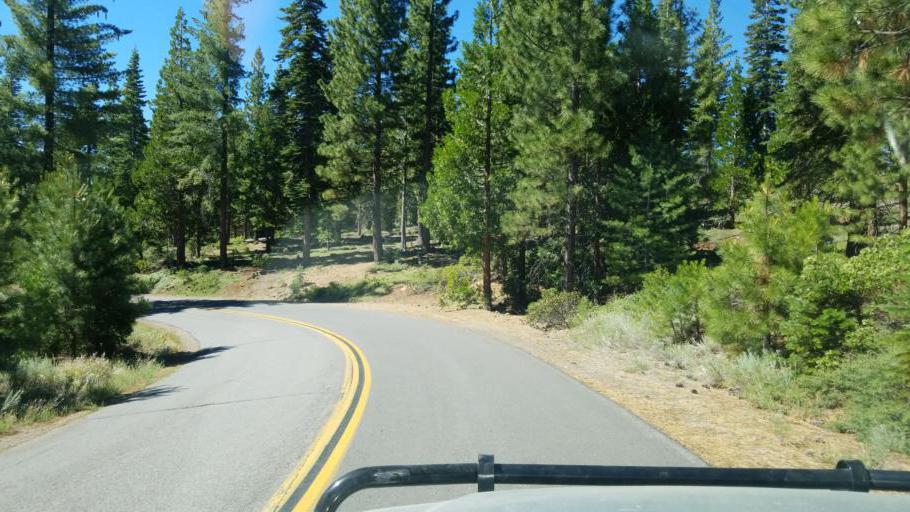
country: US
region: California
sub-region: Lassen County
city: Susanville
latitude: 40.4596
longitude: -120.7614
